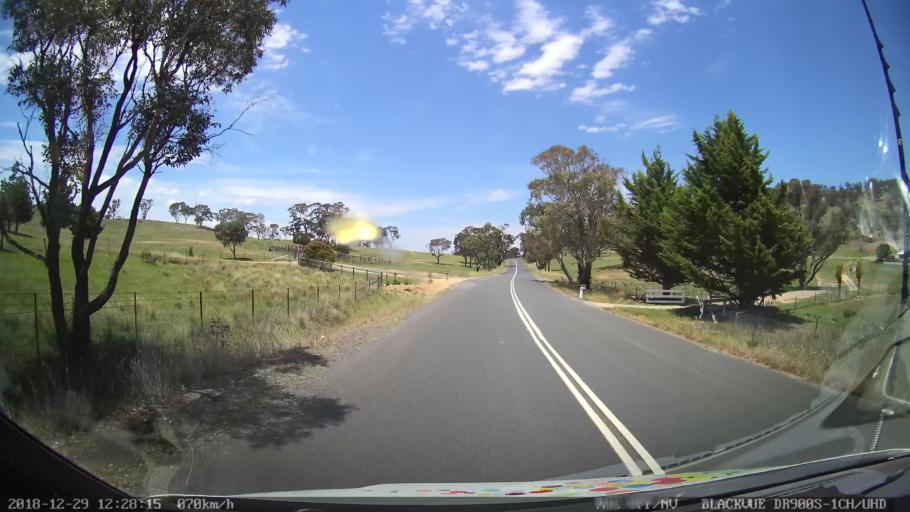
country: AU
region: Australian Capital Territory
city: Macarthur
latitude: -35.4846
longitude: 149.2257
